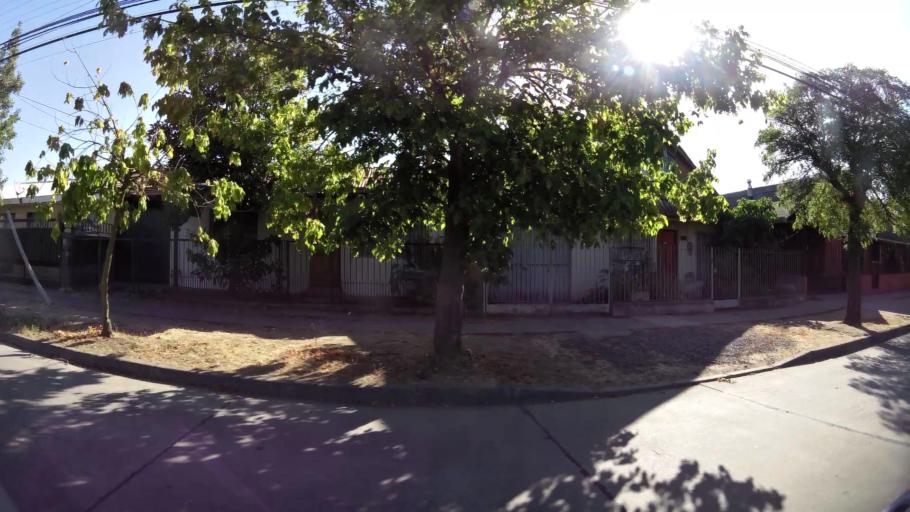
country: CL
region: Maule
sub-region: Provincia de Talca
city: Talca
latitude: -35.4420
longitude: -71.6692
